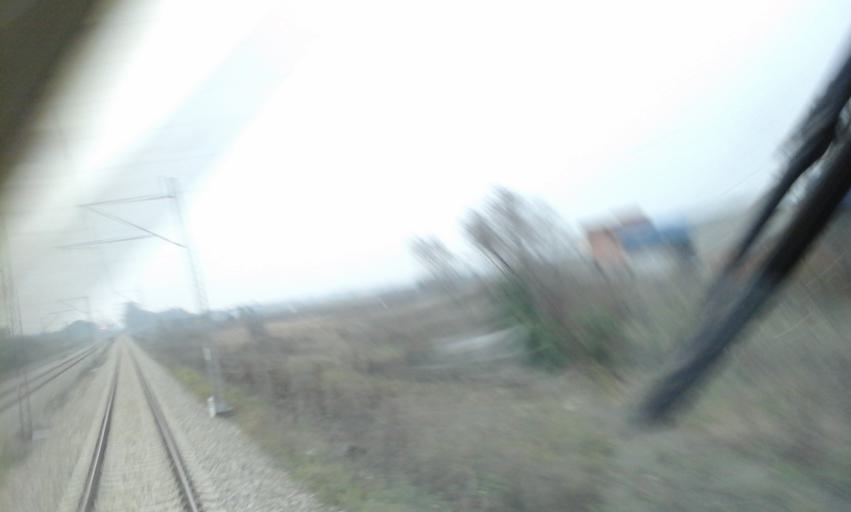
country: RS
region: Central Serbia
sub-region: Pomoravski Okrug
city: Paracin
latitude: 43.8809
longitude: 21.3871
